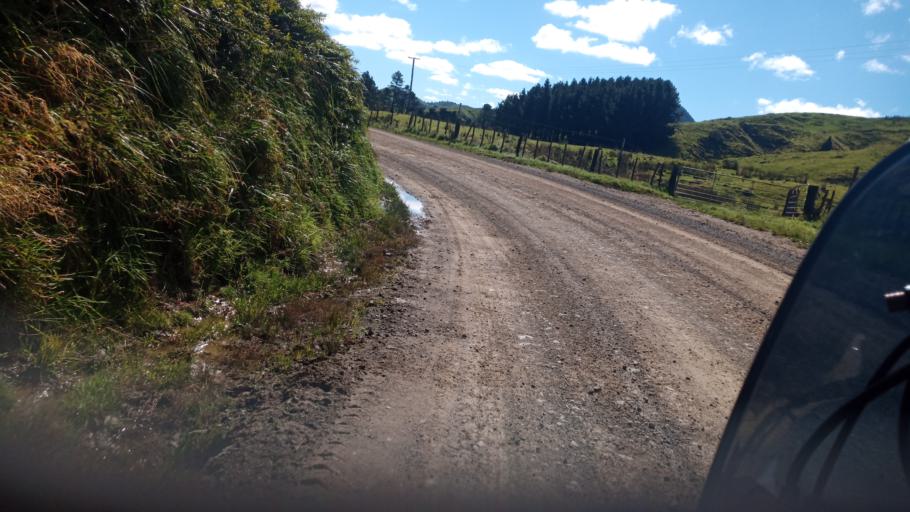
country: NZ
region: Bay of Plenty
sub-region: Opotiki District
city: Opotiki
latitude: -38.3353
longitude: 177.5786
